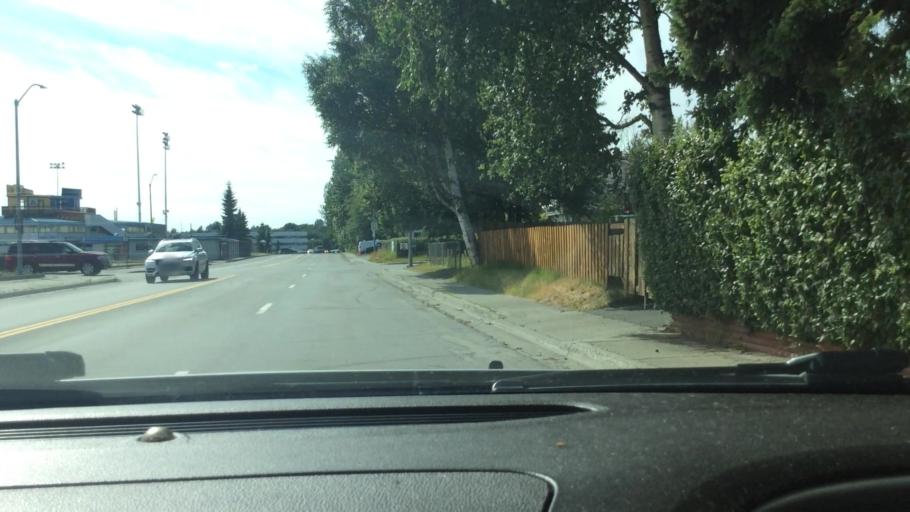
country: US
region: Alaska
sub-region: Anchorage Municipality
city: Anchorage
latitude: 61.2061
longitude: -149.8742
